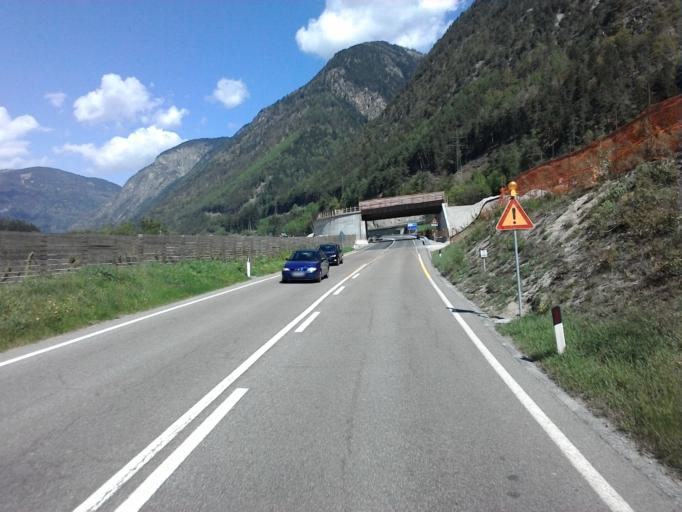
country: IT
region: Trentino-Alto Adige
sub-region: Bolzano
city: Fortezza
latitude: 46.7989
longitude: 11.5975
